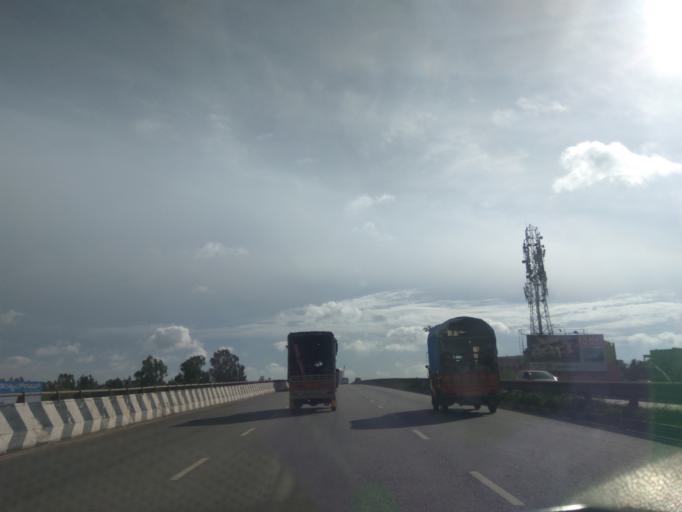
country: IN
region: Karnataka
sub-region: Bangalore Rural
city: Hoskote
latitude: 13.0451
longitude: 77.7489
